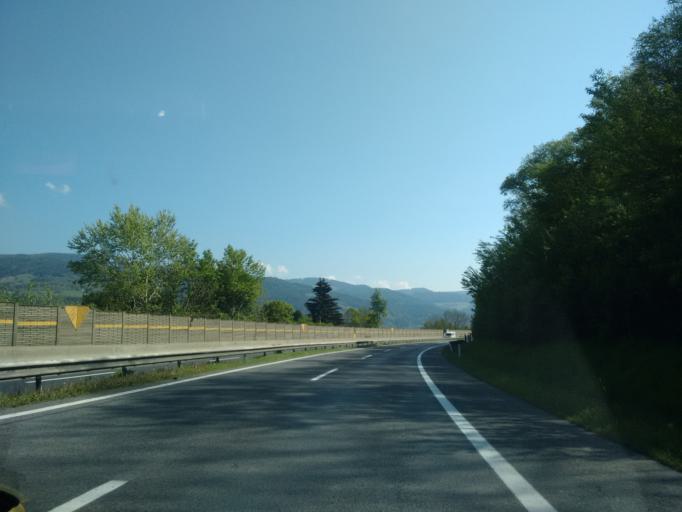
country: AT
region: Styria
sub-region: Politischer Bezirk Leoben
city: Leoben
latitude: 47.3787
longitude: 15.1124
